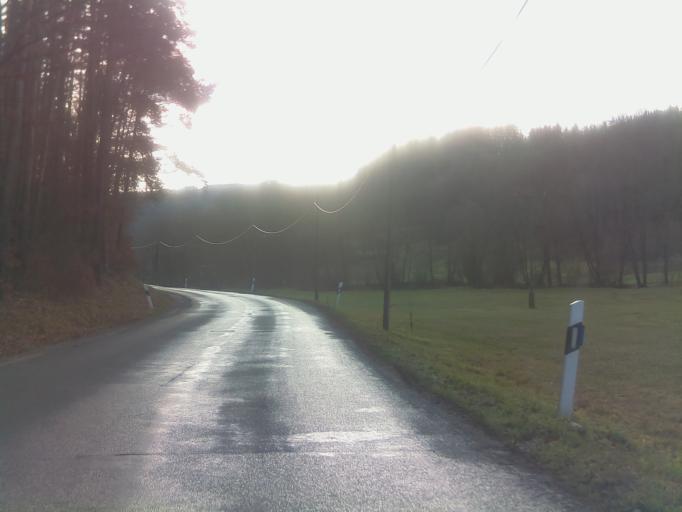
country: DE
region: Thuringia
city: Rottenbach
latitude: 50.7039
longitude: 11.1990
